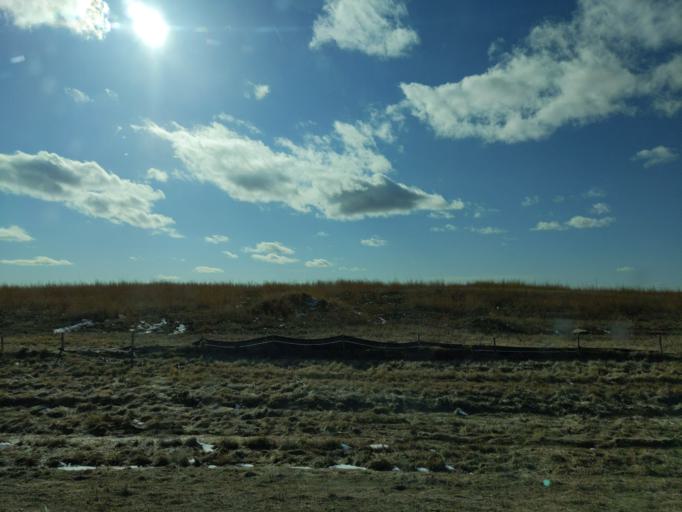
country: CA
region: Saskatchewan
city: Lloydminster
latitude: 53.3043
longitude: -110.0465
